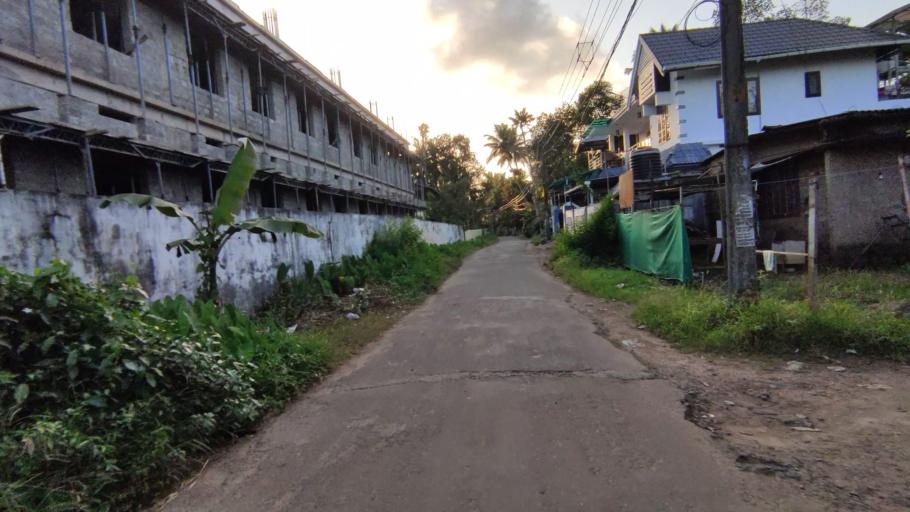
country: IN
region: Kerala
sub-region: Kottayam
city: Kottayam
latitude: 9.5953
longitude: 76.4681
